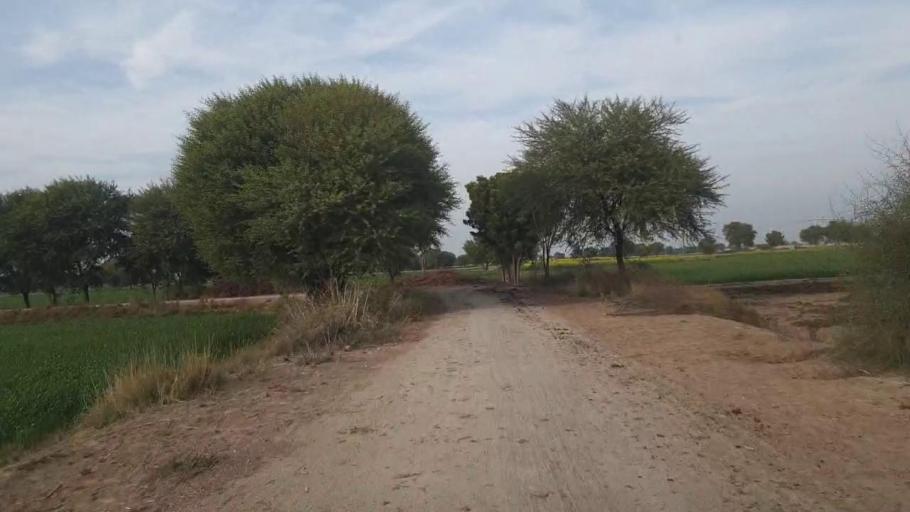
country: PK
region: Sindh
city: Shahpur Chakar
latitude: 26.1251
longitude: 68.5546
